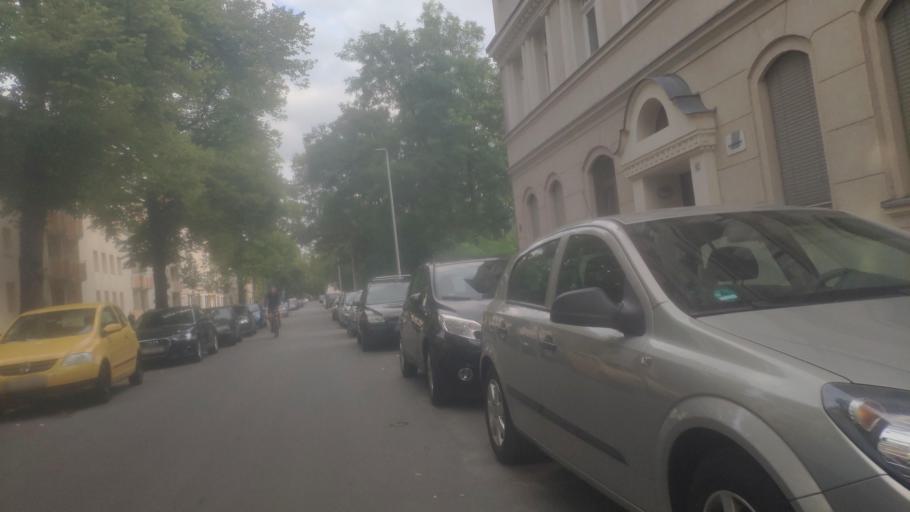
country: DE
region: Saxony
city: Chemnitz
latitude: 50.8185
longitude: 12.9351
